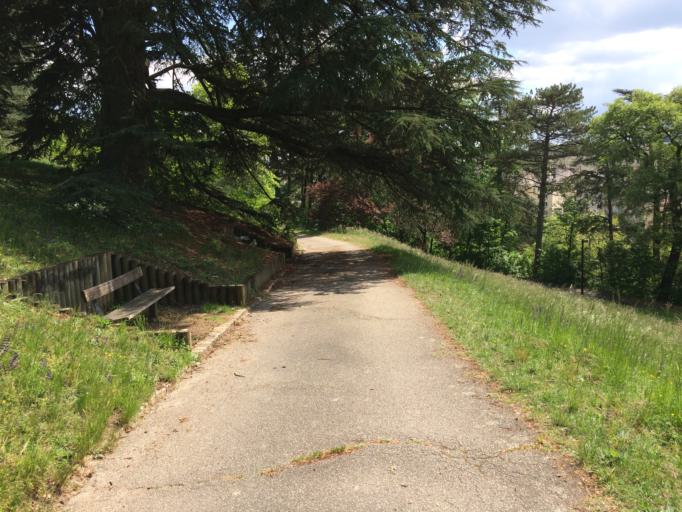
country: FR
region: Rhone-Alpes
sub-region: Departement du Rhone
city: Oullins
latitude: 45.7209
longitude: 4.8065
